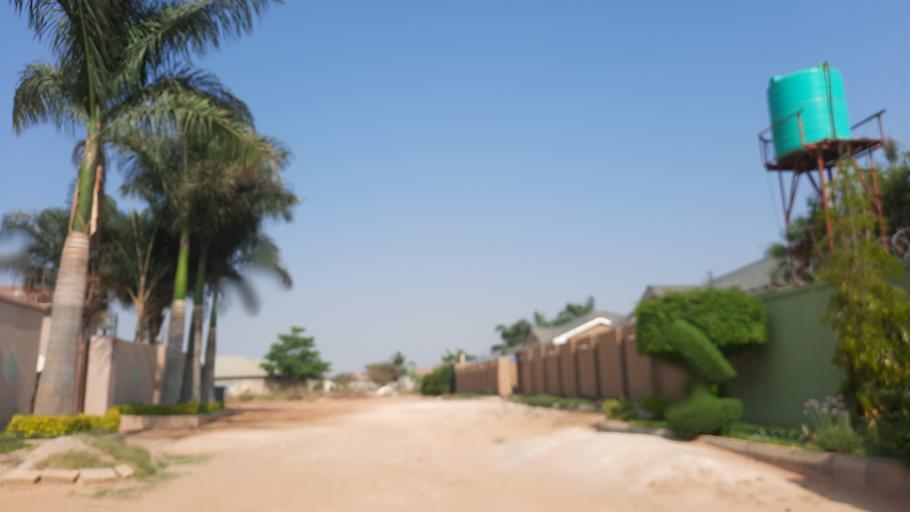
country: ZM
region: Lusaka
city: Lusaka
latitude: -15.3929
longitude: 28.3879
